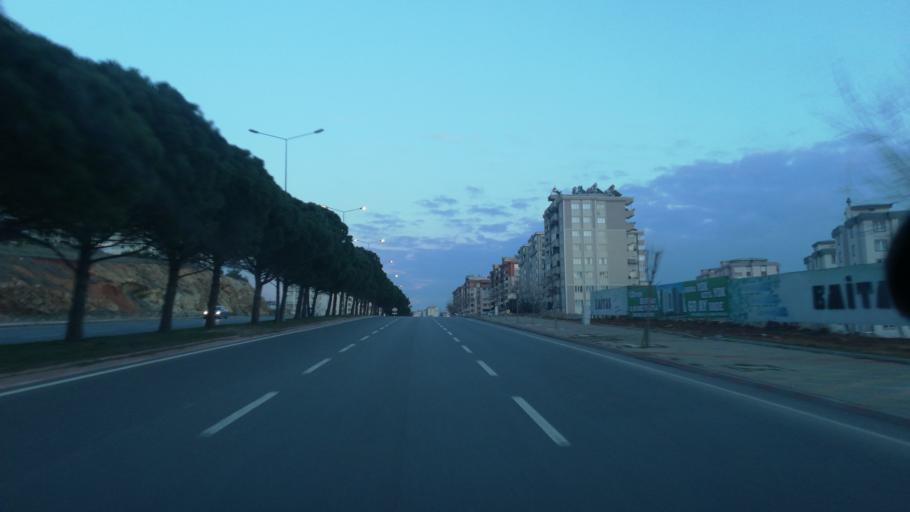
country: TR
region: Kahramanmaras
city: Kahramanmaras
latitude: 37.5967
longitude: 36.8484
